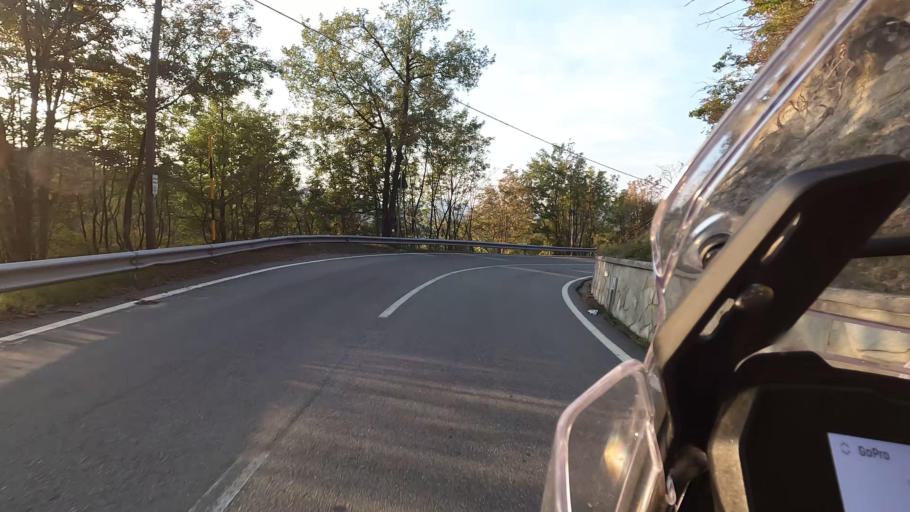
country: IT
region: Liguria
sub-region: Provincia di Savona
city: Sassello
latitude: 44.4884
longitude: 8.4974
